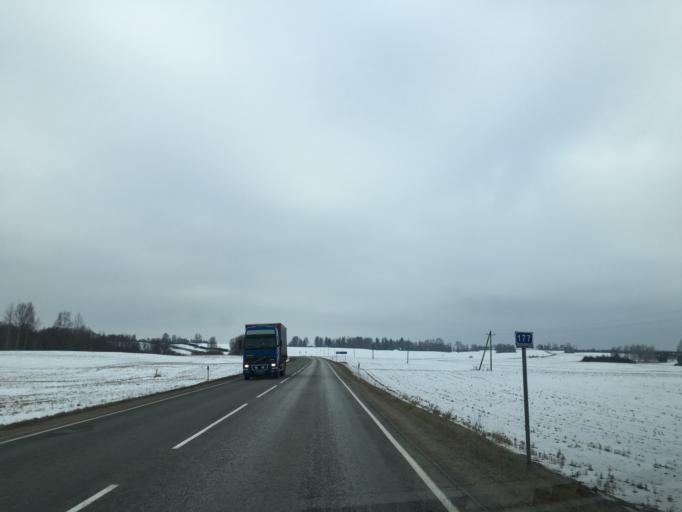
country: EE
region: Tartu
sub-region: Elva linn
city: Elva
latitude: 58.1206
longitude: 26.2410
